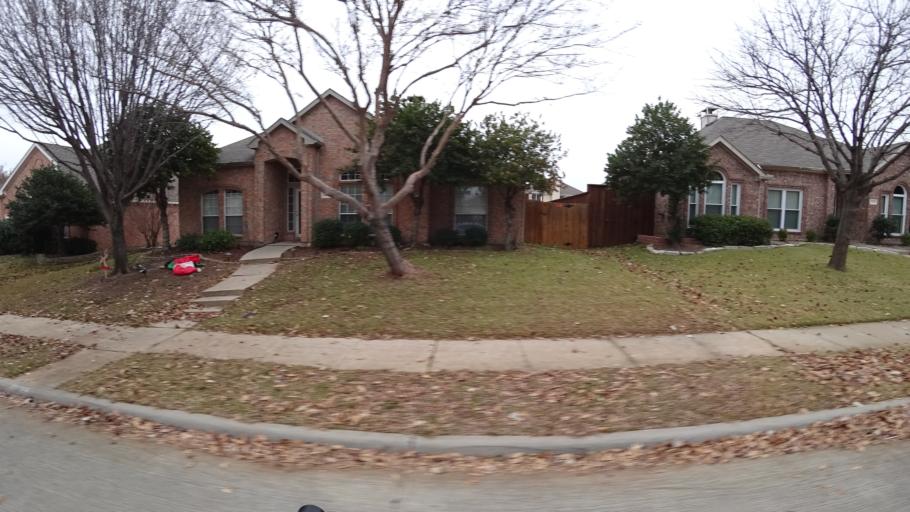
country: US
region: Texas
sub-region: Denton County
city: Highland Village
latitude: 33.0584
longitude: -97.0327
